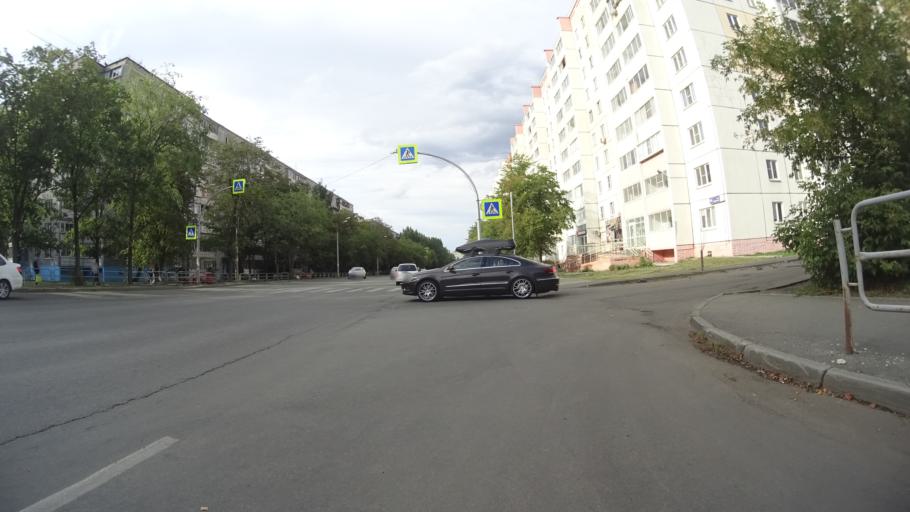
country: RU
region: Chelyabinsk
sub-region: Gorod Chelyabinsk
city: Chelyabinsk
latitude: 55.1956
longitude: 61.3179
